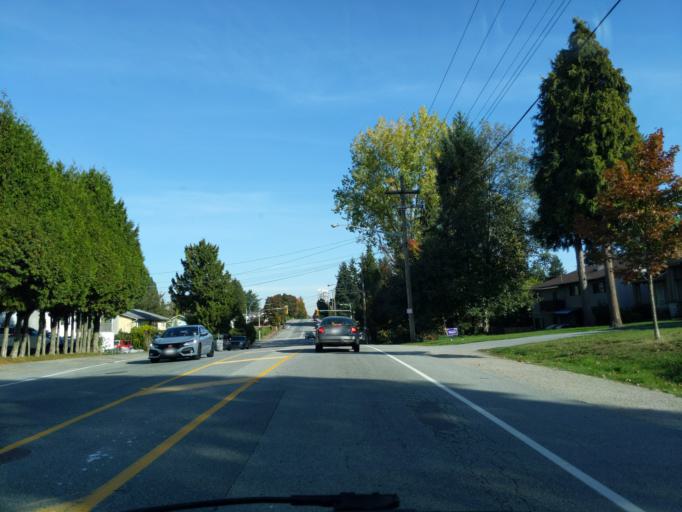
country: CA
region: British Columbia
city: New Westminster
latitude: 49.1917
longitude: -122.8696
